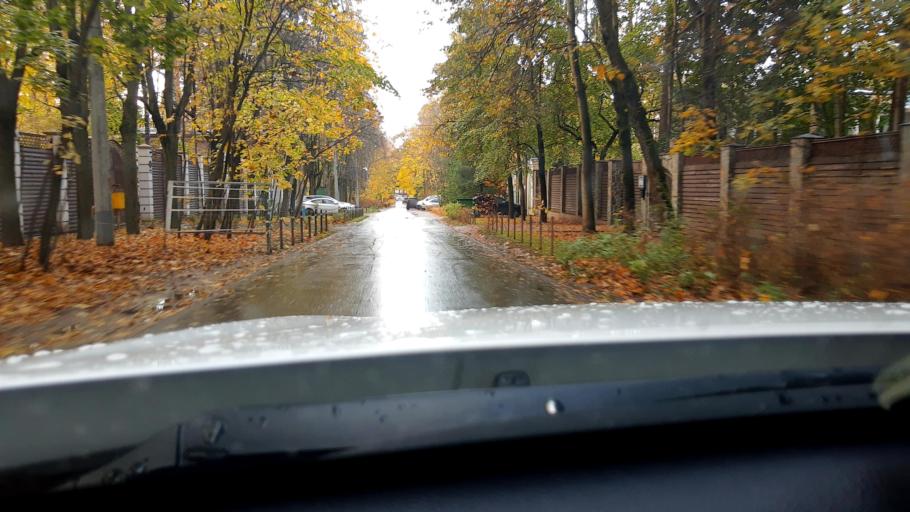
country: RU
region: Moscow
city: Shchukino
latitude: 55.7846
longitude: 37.4376
